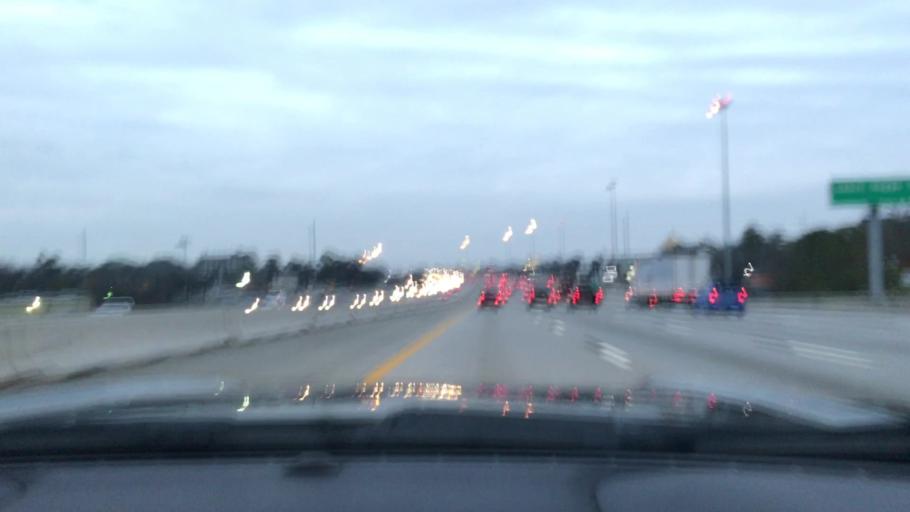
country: US
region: Texas
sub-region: Harris County
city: Houston
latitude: 29.8311
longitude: -95.3347
